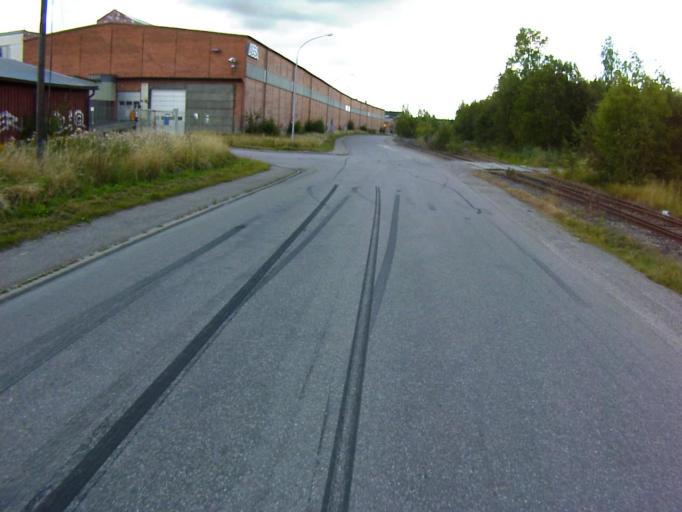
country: SE
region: Soedermanland
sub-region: Eskilstuna Kommun
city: Eskilstuna
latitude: 59.3789
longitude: 16.4850
